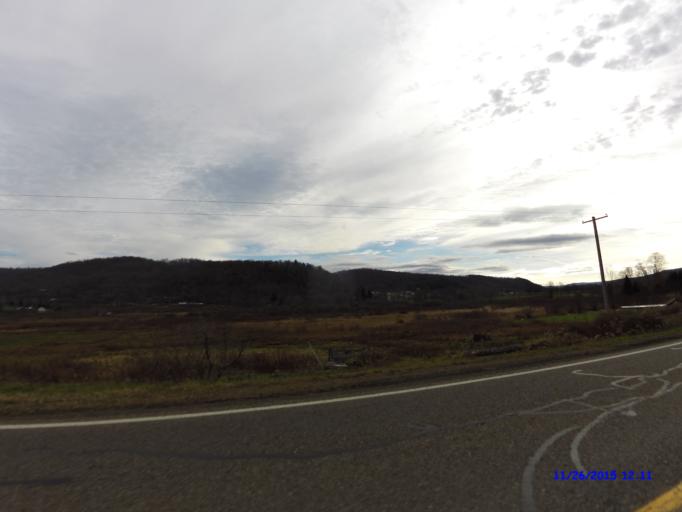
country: US
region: New York
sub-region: Cattaraugus County
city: Allegany
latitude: 42.1827
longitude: -78.5035
